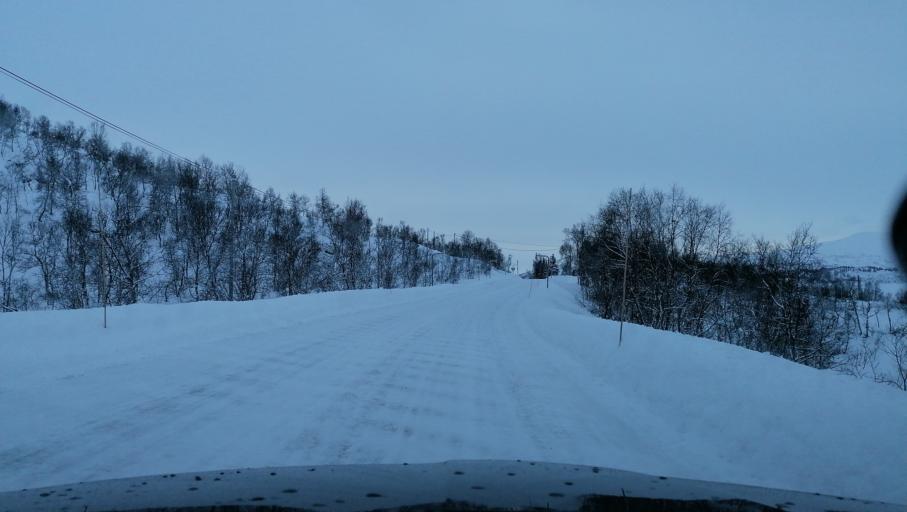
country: NO
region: Aust-Agder
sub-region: Bykle
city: Hovden
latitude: 59.6416
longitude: 7.4570
